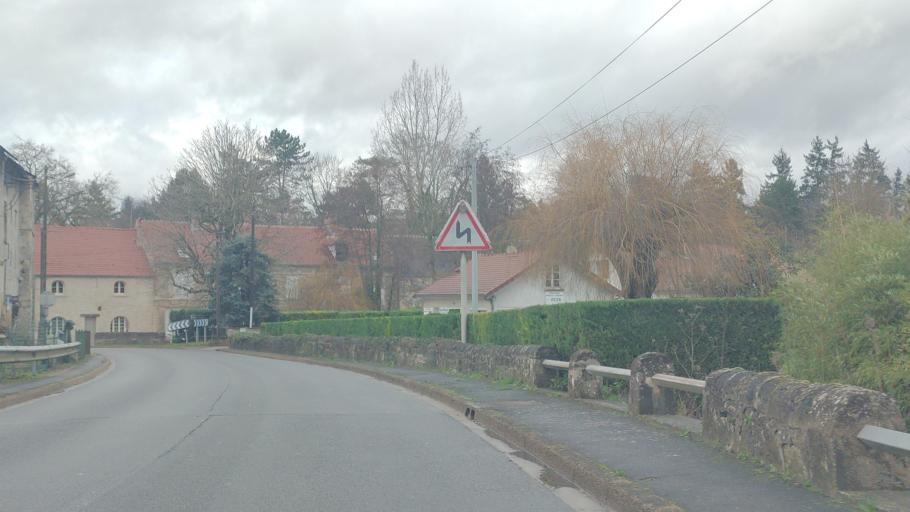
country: FR
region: Picardie
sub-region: Departement de l'Oise
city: Orry-la-Ville
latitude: 49.1531
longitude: 2.5236
